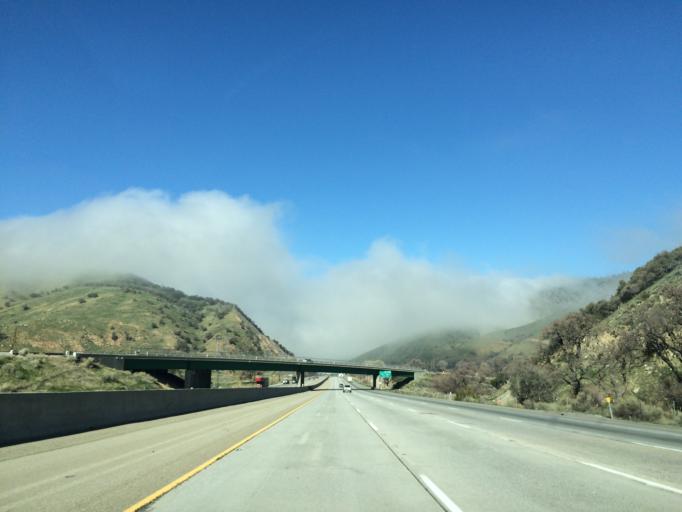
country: US
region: California
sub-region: Kern County
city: Lebec
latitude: 34.8646
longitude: -118.8818
